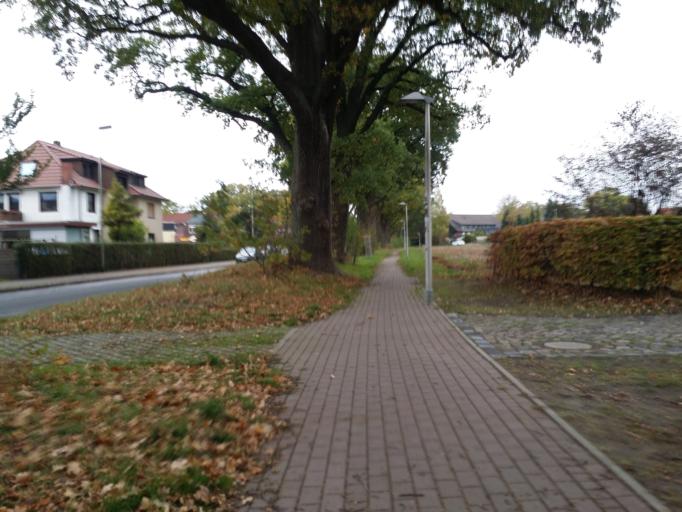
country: DE
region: Lower Saxony
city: Delmenhorst
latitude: 53.0545
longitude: 8.6791
